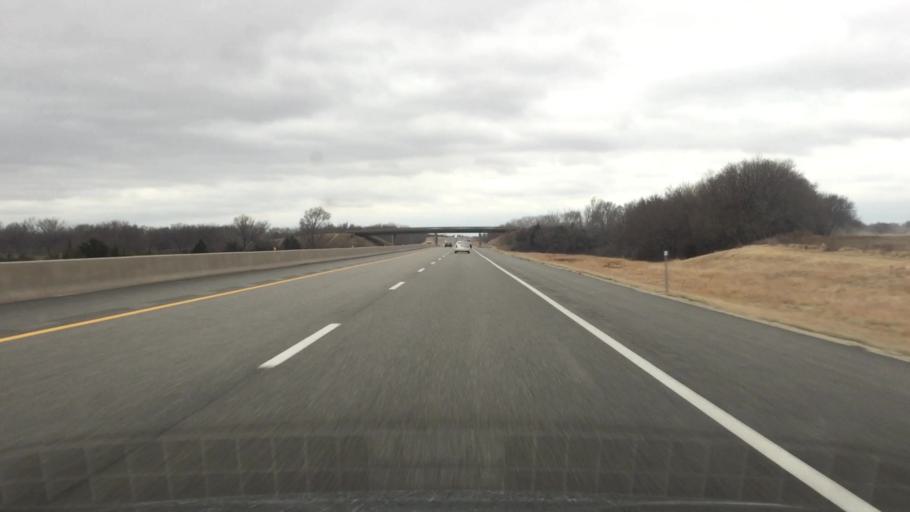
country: US
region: Kansas
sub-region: Butler County
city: Towanda
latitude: 37.7559
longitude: -97.0141
